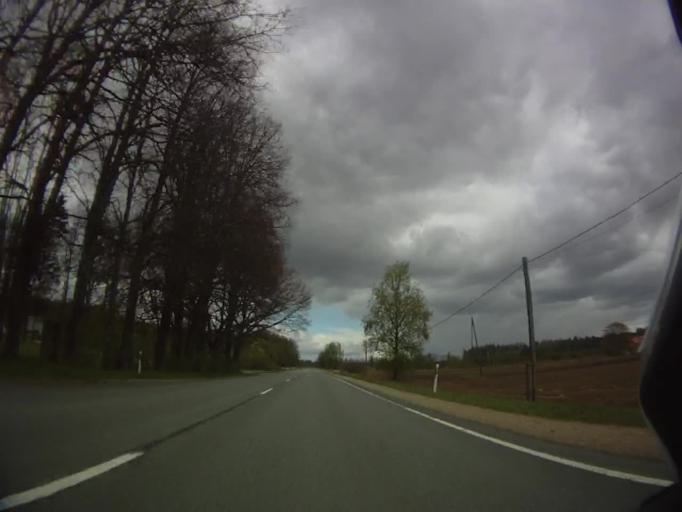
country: LV
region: Pargaujas
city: Stalbe
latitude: 57.3356
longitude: 24.9278
